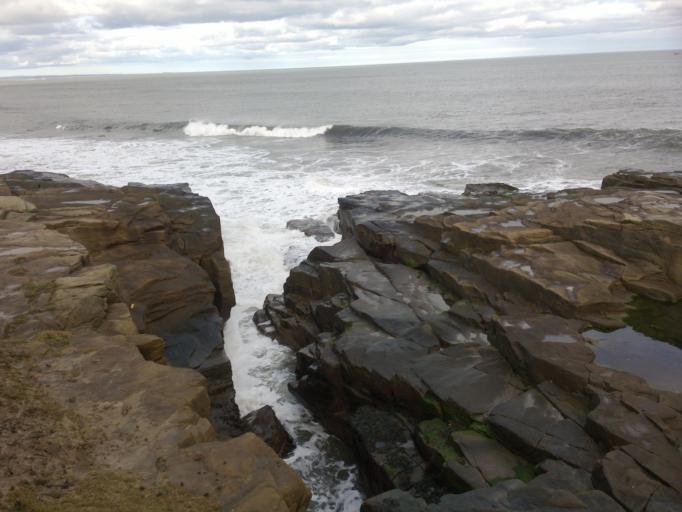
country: GB
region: England
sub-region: Northumberland
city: Newbiggin-by-the-Sea
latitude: 55.1980
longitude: -1.5062
